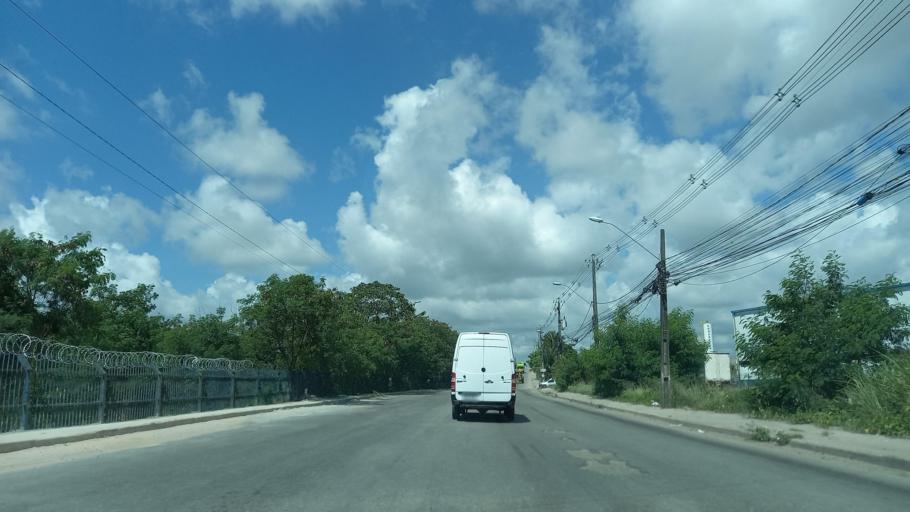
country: BR
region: Pernambuco
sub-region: Jaboatao Dos Guararapes
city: Jaboatao
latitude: -8.1554
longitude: -34.9475
